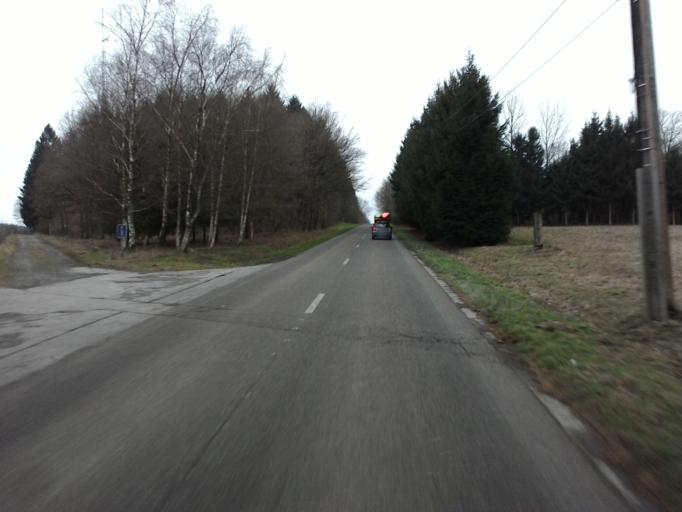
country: BE
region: Wallonia
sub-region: Province de Namur
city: Gedinne
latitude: 50.0378
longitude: 4.9524
